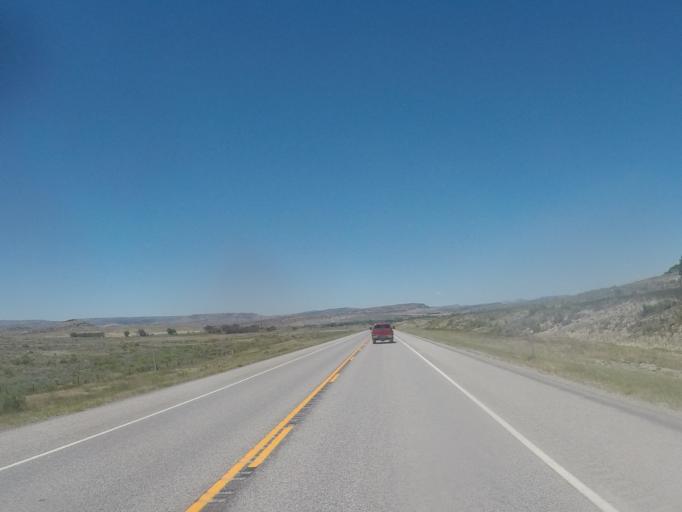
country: US
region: Montana
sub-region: Carbon County
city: Red Lodge
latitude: 45.2249
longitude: -108.8837
